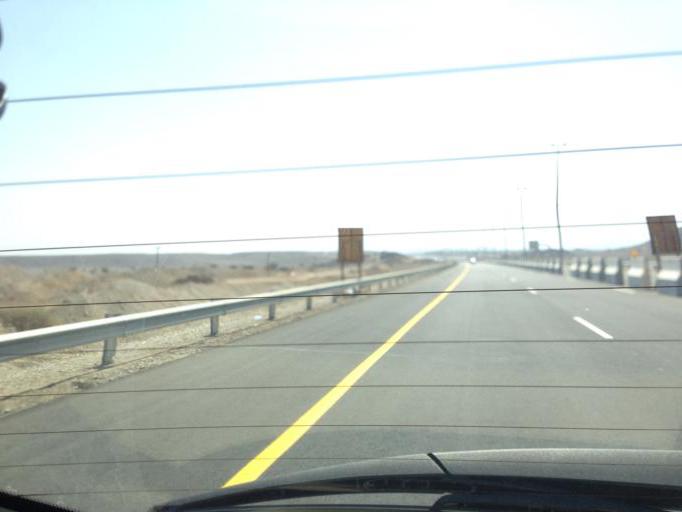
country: OM
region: Al Batinah
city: Rustaq
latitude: 23.5574
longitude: 57.5008
